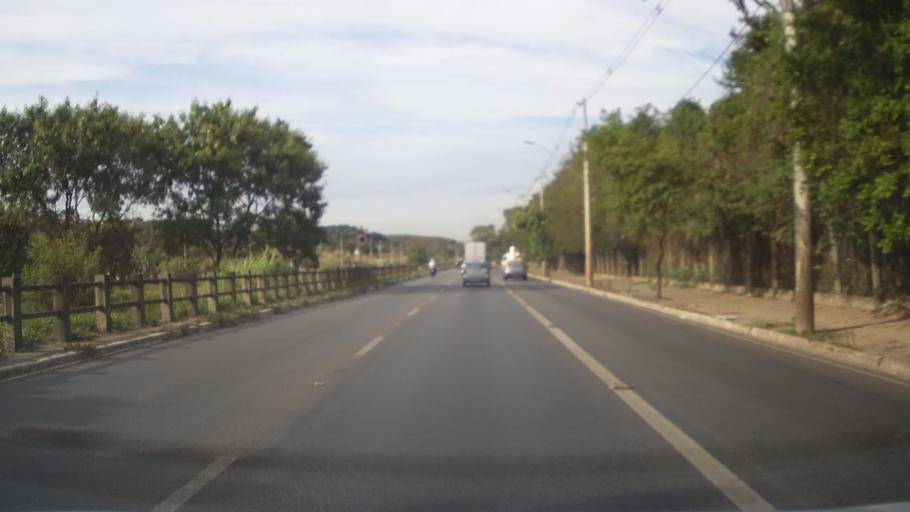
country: BR
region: Minas Gerais
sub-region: Contagem
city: Contagem
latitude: -19.8900
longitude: -44.0387
